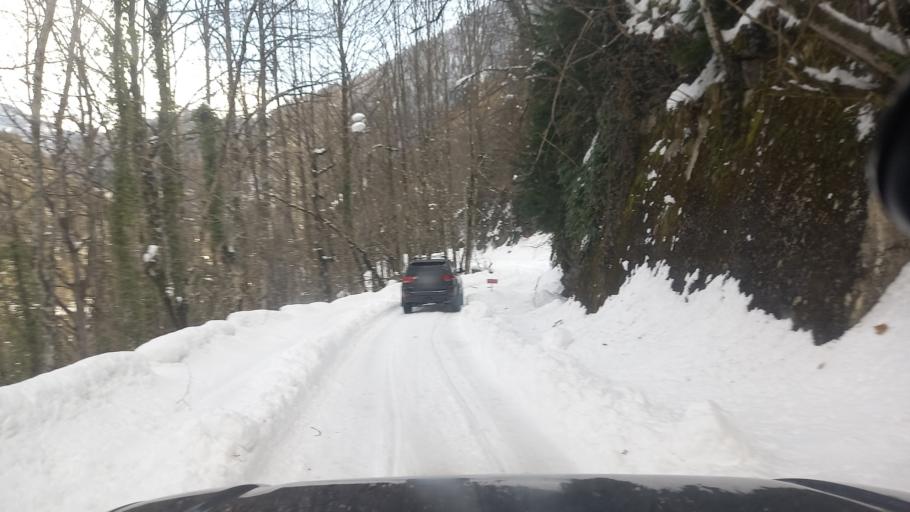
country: GE
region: Abkhazia
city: Gagra
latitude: 43.4790
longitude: 40.5515
